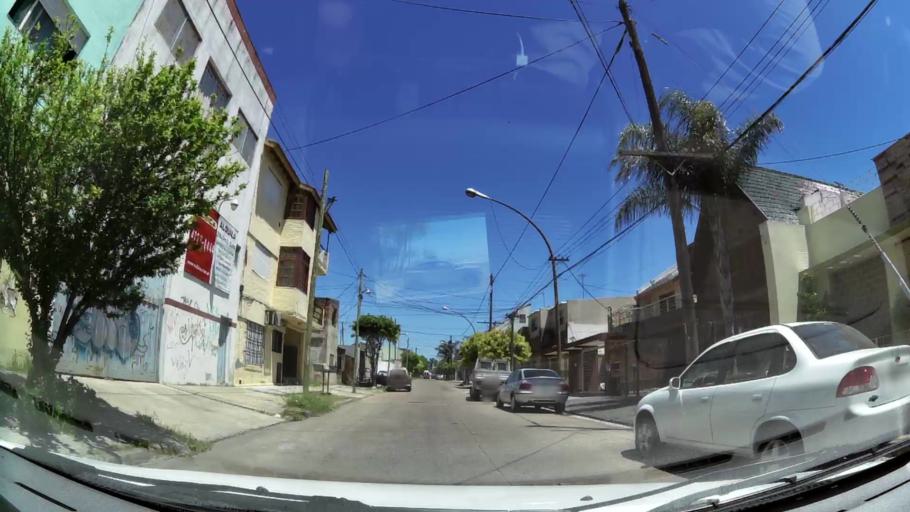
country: AR
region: Buenos Aires
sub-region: Partido de General San Martin
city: General San Martin
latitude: -34.5851
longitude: -58.5421
